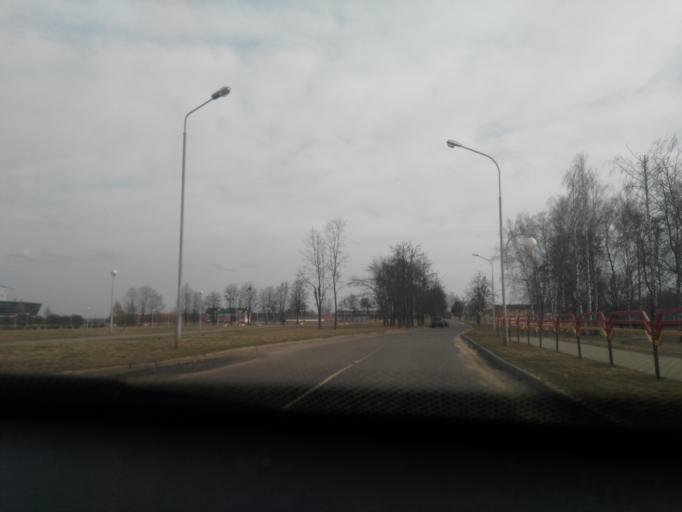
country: BY
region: Mogilev
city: Babruysk
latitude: 53.1422
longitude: 29.2424
